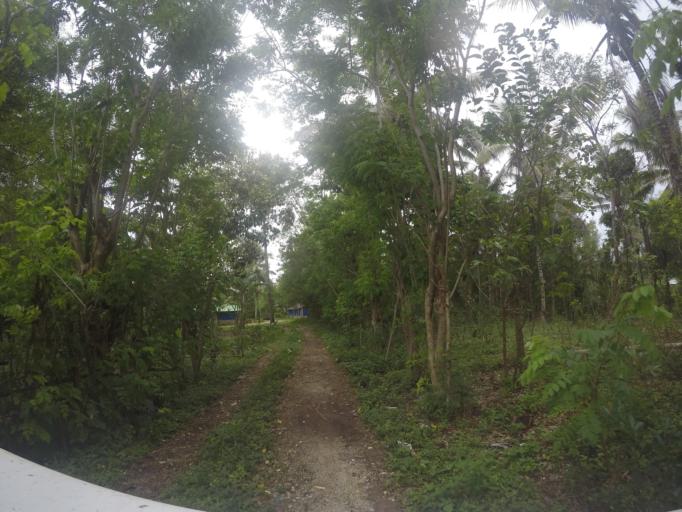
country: TL
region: Lautem
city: Lospalos
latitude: -8.5276
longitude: 126.9923
